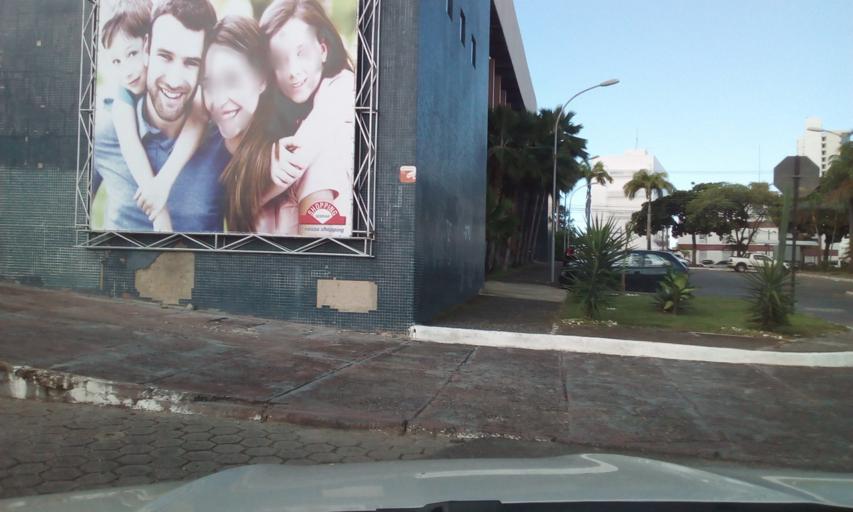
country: BR
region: Paraiba
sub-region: Joao Pessoa
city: Joao Pessoa
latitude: -7.1115
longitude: -34.8562
